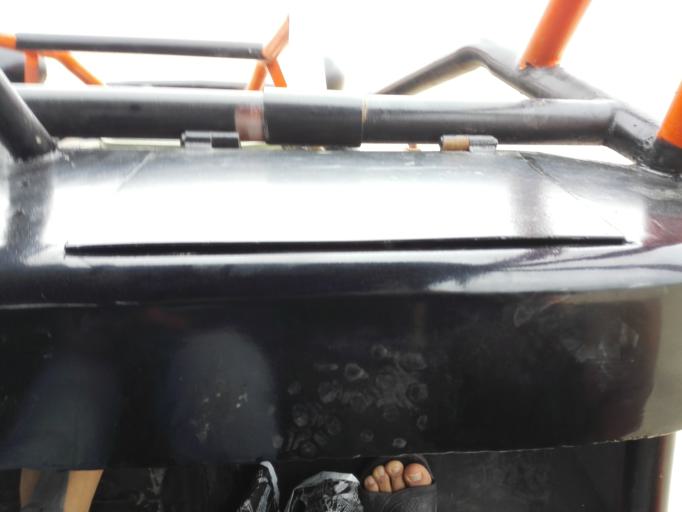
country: PE
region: Ica
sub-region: Provincia de Ica
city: Ica
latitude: -14.0869
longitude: -75.7725
